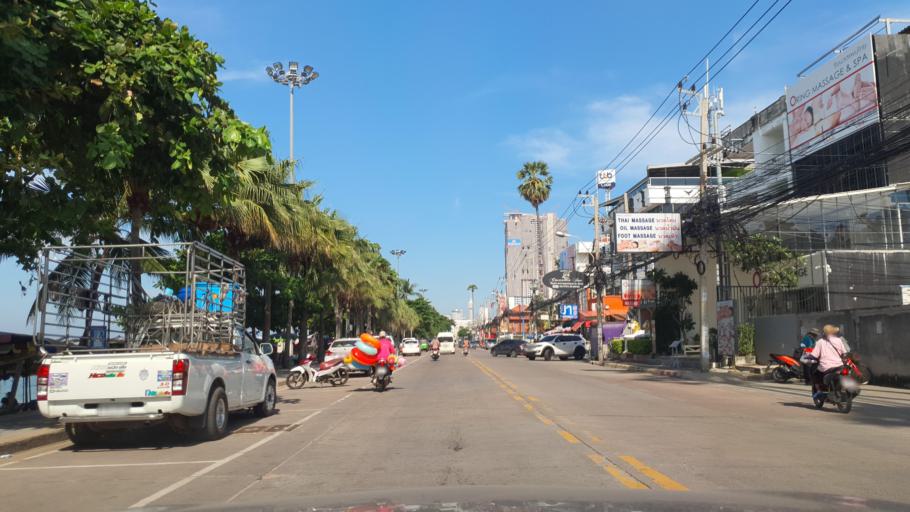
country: TH
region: Chon Buri
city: Phatthaya
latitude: 12.8835
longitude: 100.8802
